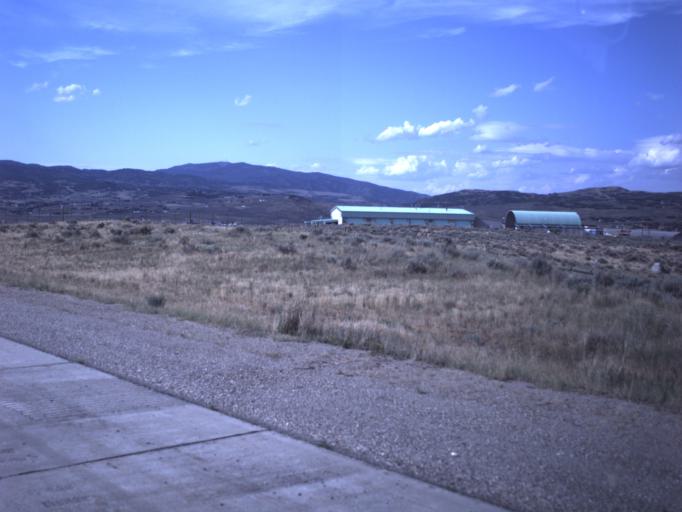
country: US
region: Utah
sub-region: Summit County
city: Park City
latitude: 40.7089
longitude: -111.4799
